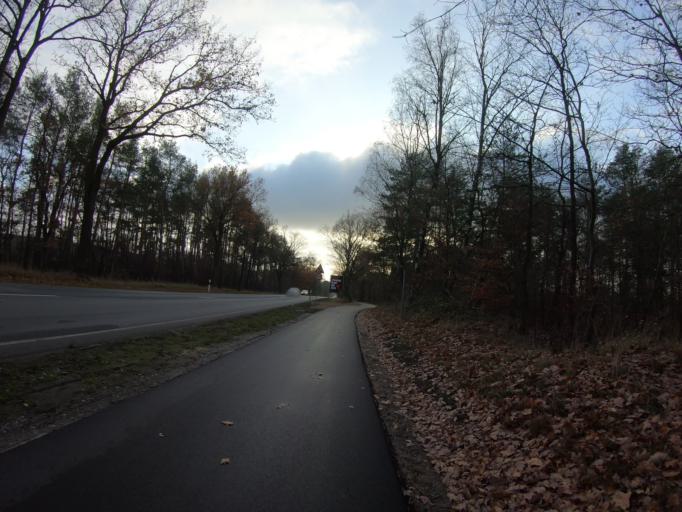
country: DE
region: Lower Saxony
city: Wesendorf
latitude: 52.5723
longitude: 10.5225
